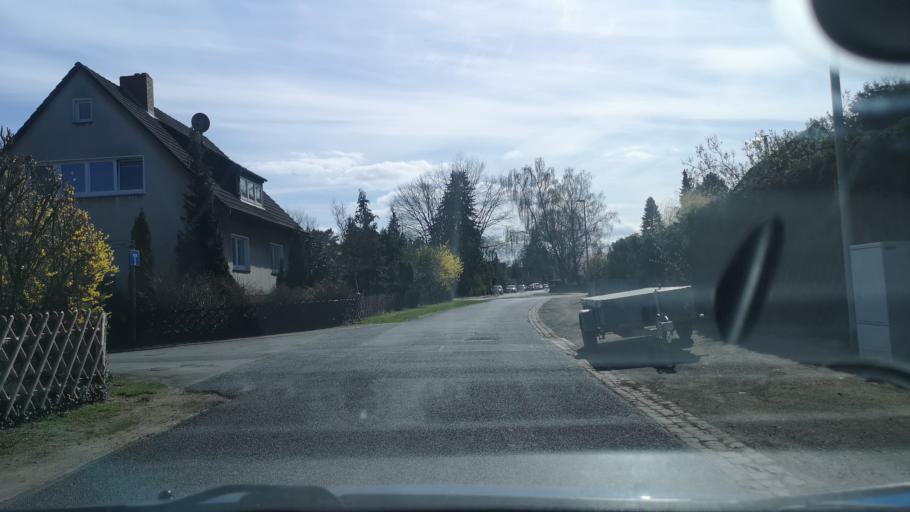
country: DE
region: Lower Saxony
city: Langenhagen
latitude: 52.4364
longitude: 9.7934
